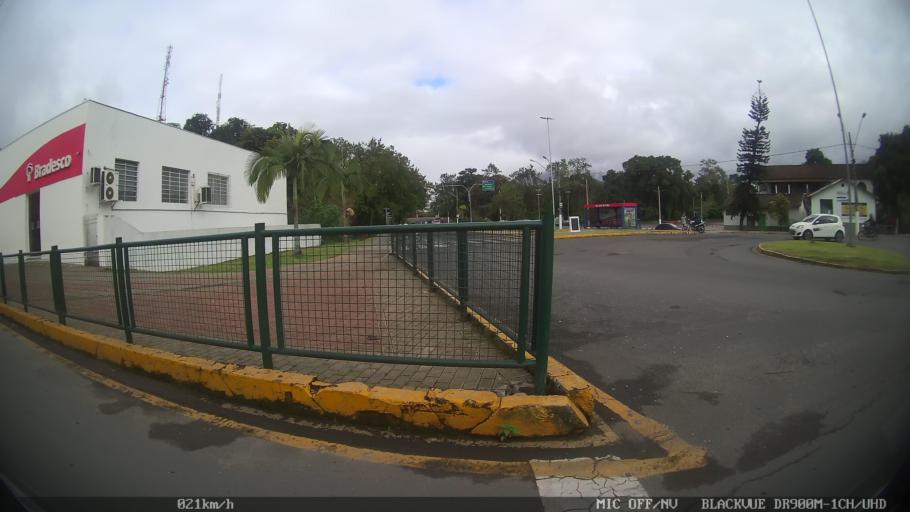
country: BR
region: Sao Paulo
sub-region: Cajati
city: Cajati
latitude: -24.7270
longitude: -48.1145
